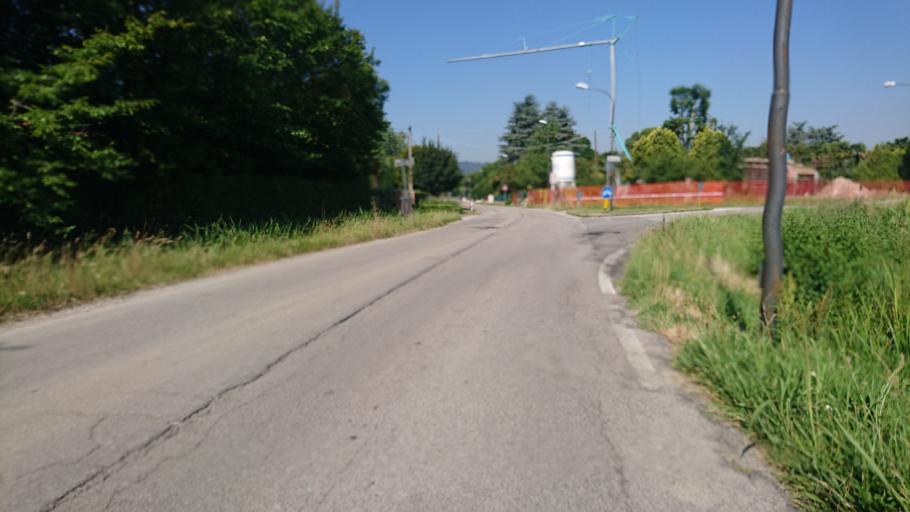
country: IT
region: Veneto
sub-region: Provincia di Padova
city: Abano Terme
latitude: 45.3586
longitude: 11.7705
